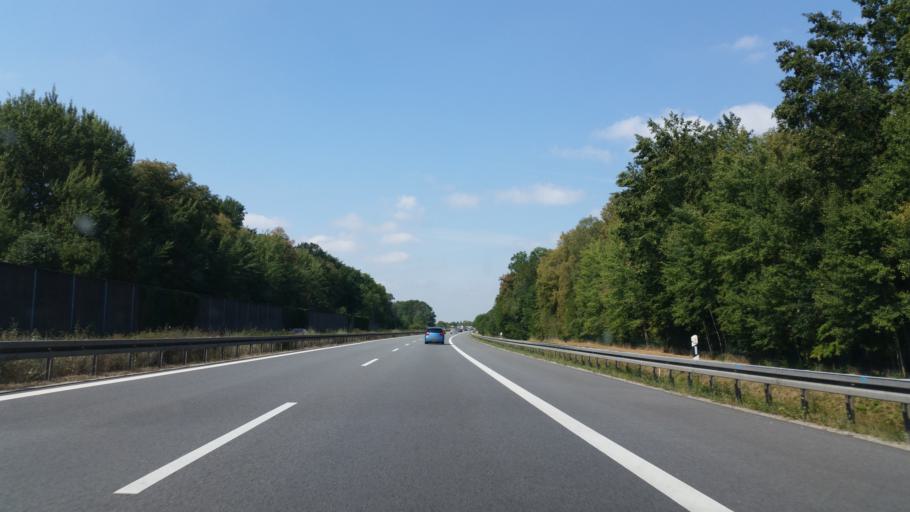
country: DE
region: Saxony
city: Malschwitz
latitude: 51.2064
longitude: 14.5218
